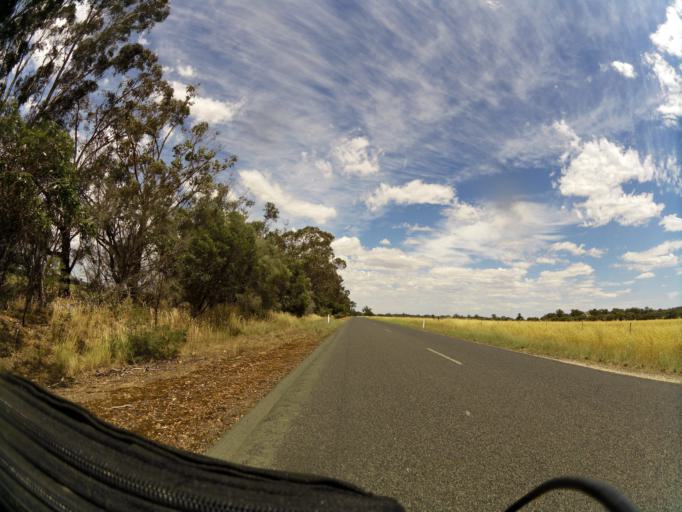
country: AU
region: Victoria
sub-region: Campaspe
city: Kyabram
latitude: -36.7669
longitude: 145.1079
